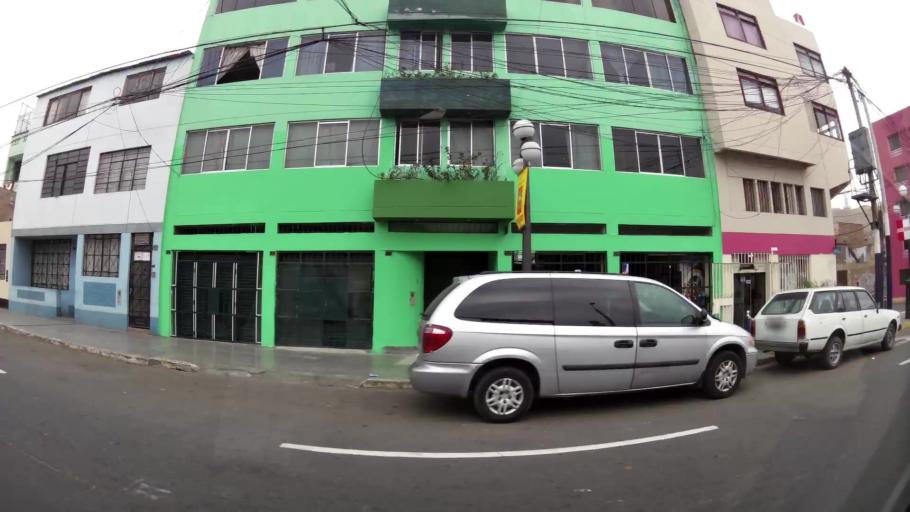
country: PE
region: Lima
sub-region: Lima
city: Surco
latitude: -12.1689
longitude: -77.0277
